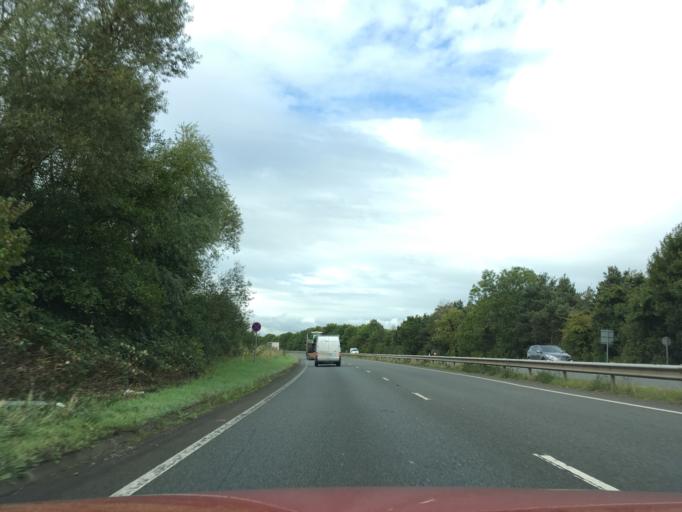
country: GB
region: England
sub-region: Gloucestershire
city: Barnwood
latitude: 51.8849
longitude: -2.2138
